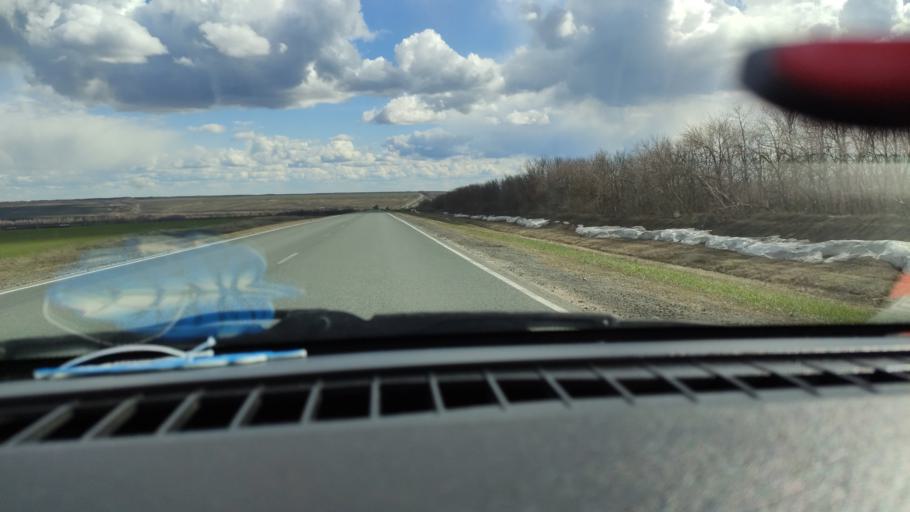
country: RU
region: Saratov
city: Dukhovnitskoye
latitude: 52.7574
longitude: 48.2436
